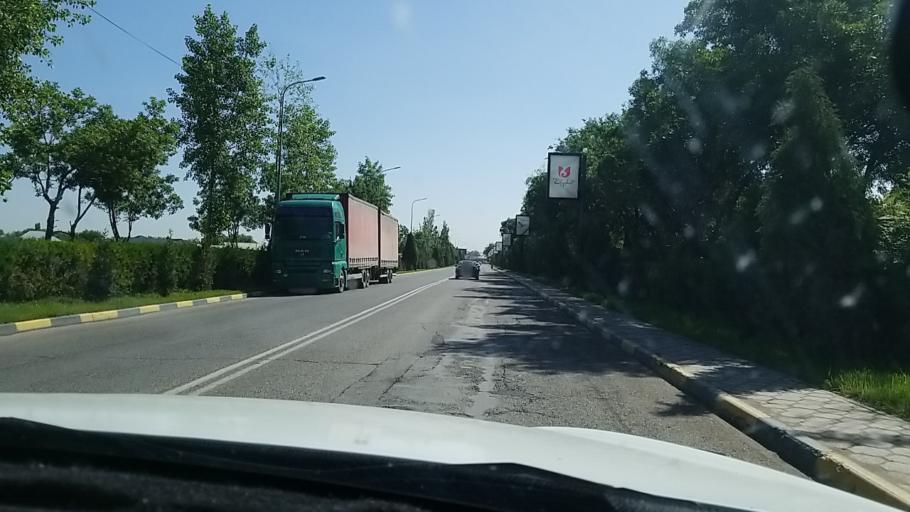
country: KZ
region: Ongtustik Qazaqstan
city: Shymkent
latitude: 42.3670
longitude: 69.4958
